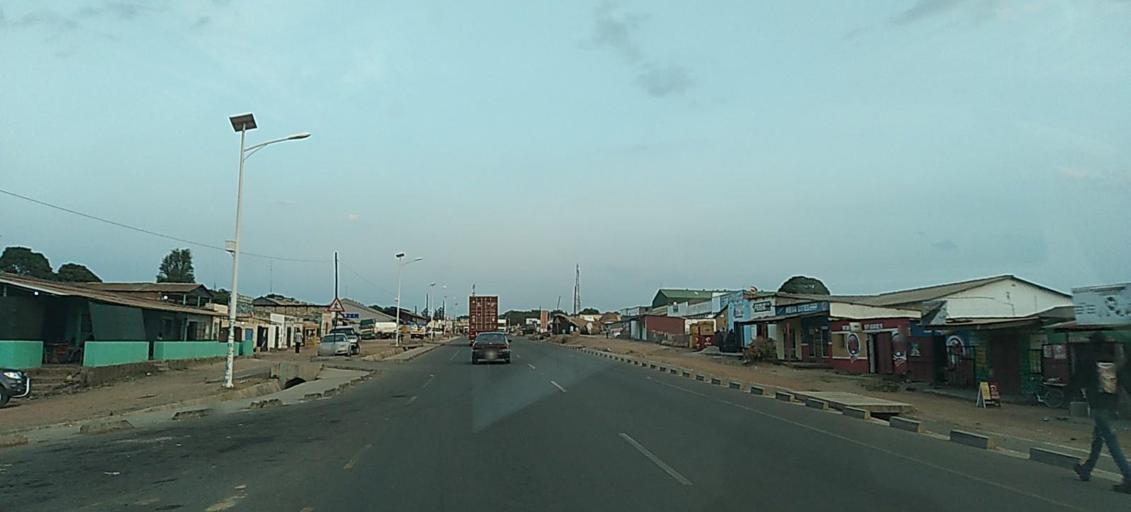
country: ZM
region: Copperbelt
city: Chingola
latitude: -12.5449
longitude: 27.8504
